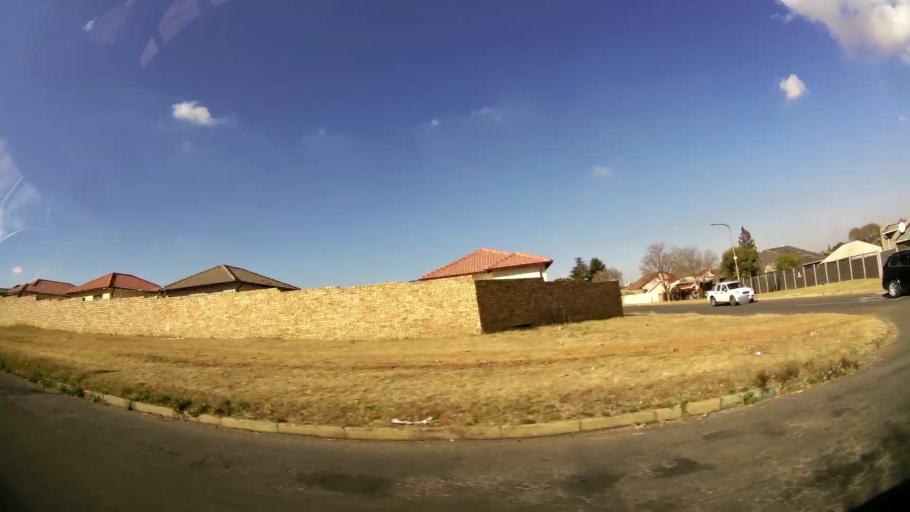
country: ZA
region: Gauteng
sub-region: City of Johannesburg Metropolitan Municipality
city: Roodepoort
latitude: -26.1395
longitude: 27.8223
